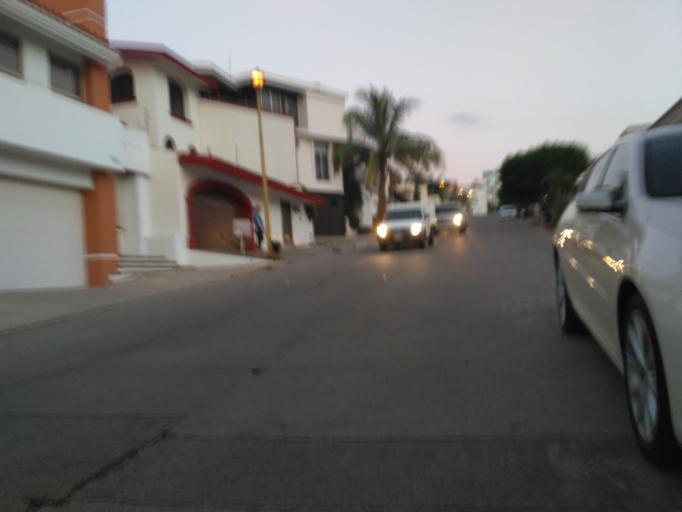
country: MX
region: Sinaloa
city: Culiacan
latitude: 24.7846
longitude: -107.3926
